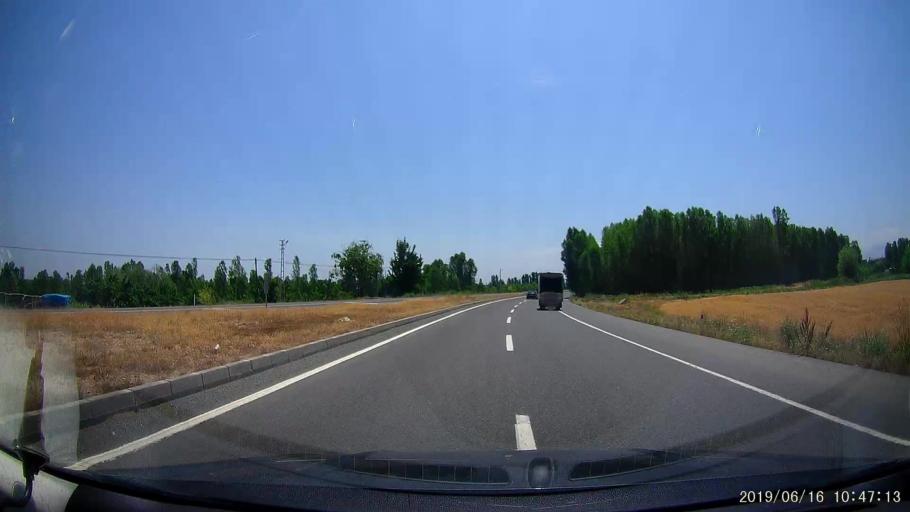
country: AM
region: Armavir
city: Shenavan
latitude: 40.0138
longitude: 43.8870
